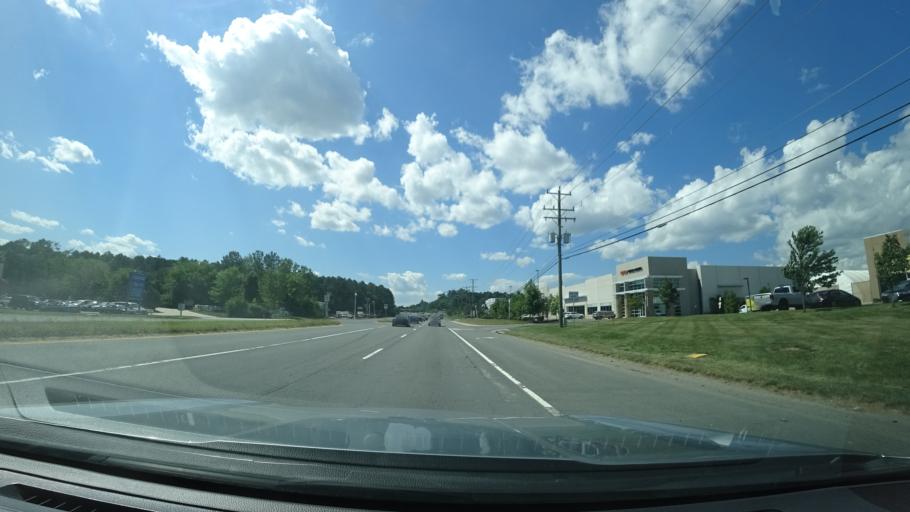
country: US
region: Virginia
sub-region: Loudoun County
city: Sterling
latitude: 38.9851
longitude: -77.4499
